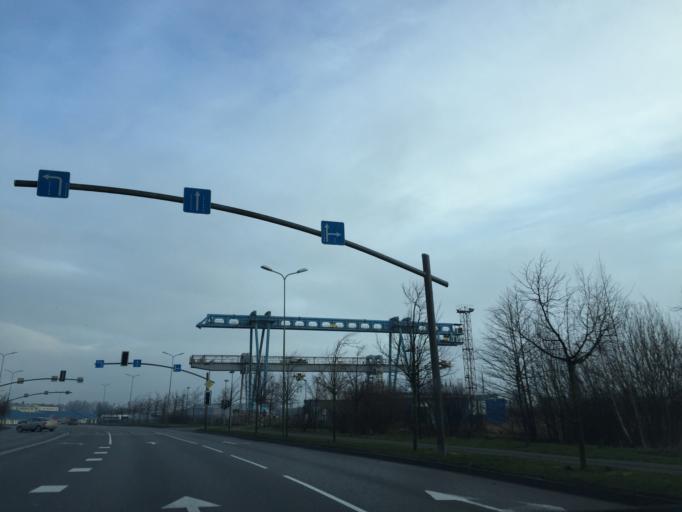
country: LV
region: Liepaja
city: Liepaja
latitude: 56.5191
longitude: 21.0267
